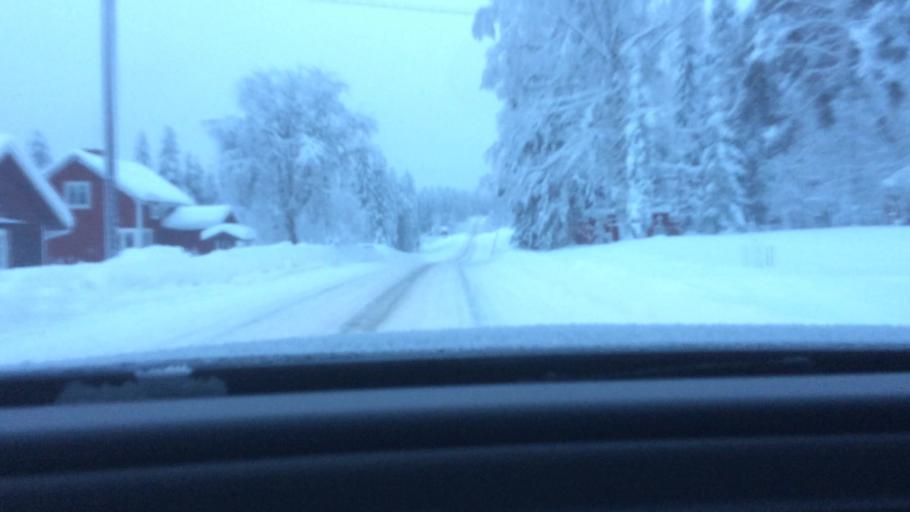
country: SE
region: Gaevleborg
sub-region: Ljusdals Kommun
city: Farila
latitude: 61.7734
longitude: 15.1708
